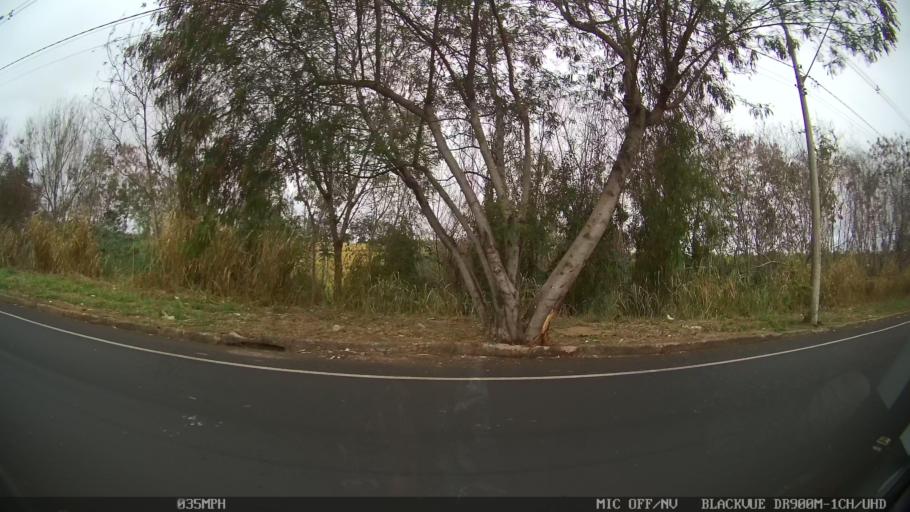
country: BR
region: Sao Paulo
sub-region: Sao Jose Do Rio Preto
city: Sao Jose do Rio Preto
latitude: -20.8261
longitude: -49.4329
